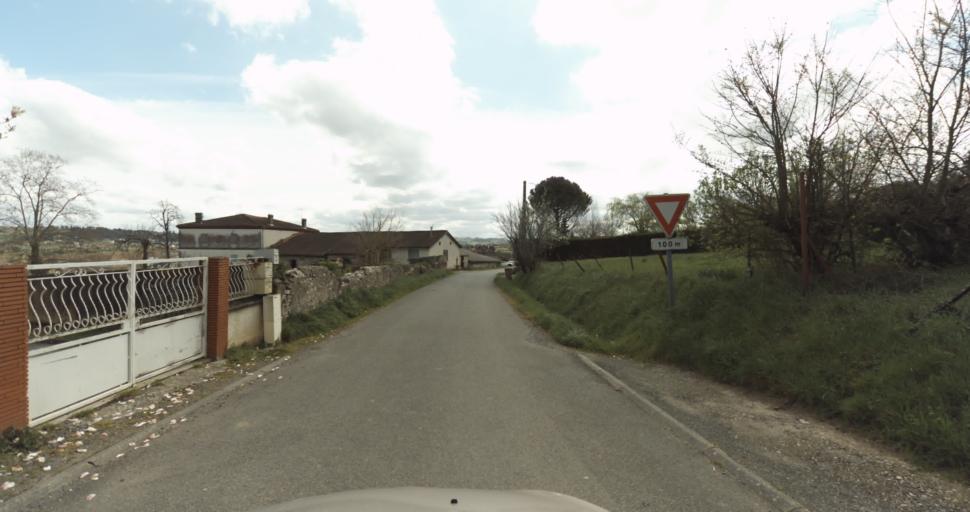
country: FR
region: Midi-Pyrenees
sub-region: Departement du Tarn
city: Puygouzon
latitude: 43.8950
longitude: 2.1475
